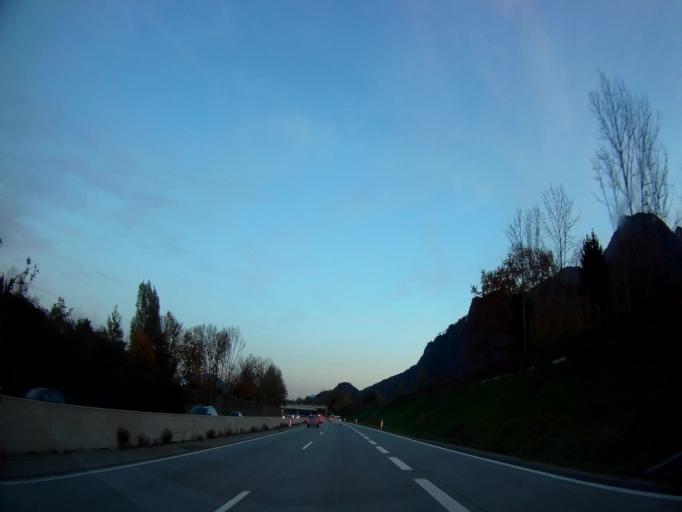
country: AT
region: Salzburg
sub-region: Politischer Bezirk Salzburg-Umgebung
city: Grodig
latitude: 47.7540
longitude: 13.0101
